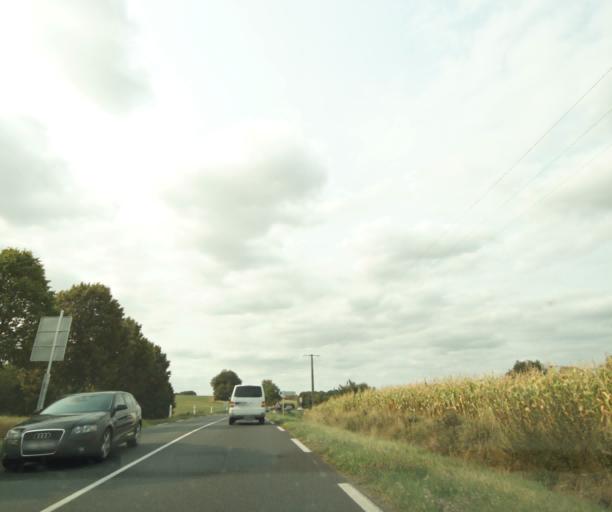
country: FR
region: Centre
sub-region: Departement de l'Indre
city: Chatillon-sur-Indre
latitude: 47.0313
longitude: 1.0967
